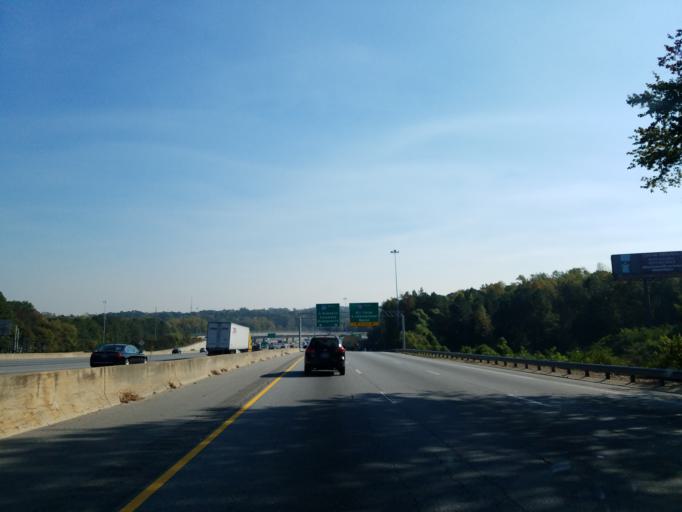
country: US
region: Georgia
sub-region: Fulton County
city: Hapeville
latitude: 33.6923
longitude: -84.4034
